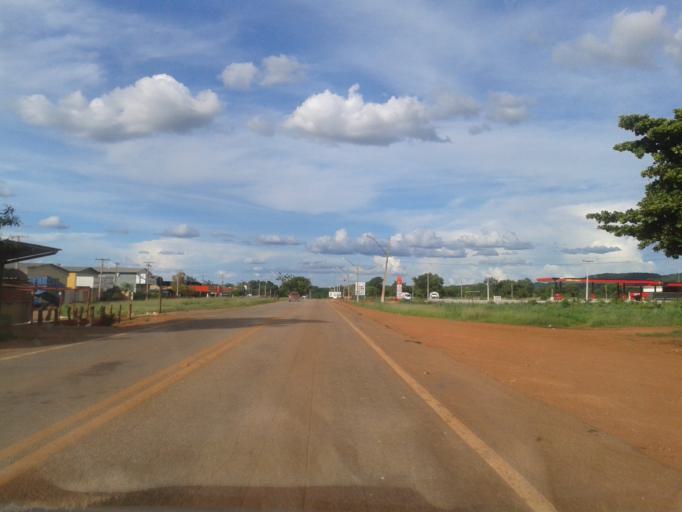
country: BR
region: Goias
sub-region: Crixas
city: Crixas
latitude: -14.1121
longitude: -50.3428
